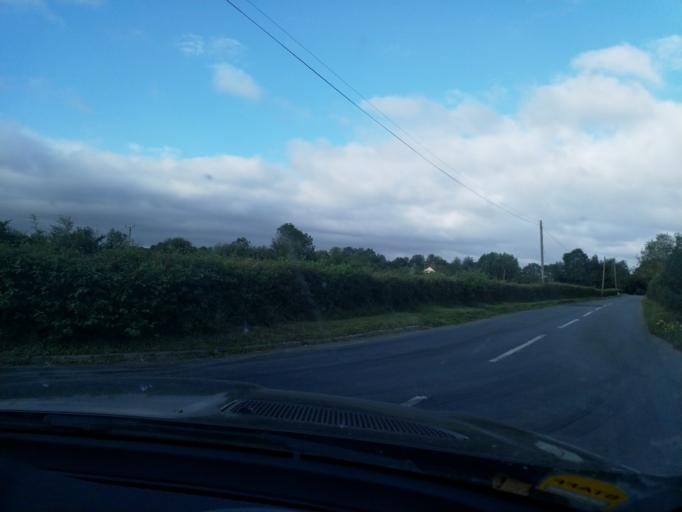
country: GB
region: England
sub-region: Suffolk
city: Stowmarket
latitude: 52.2338
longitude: 0.9702
